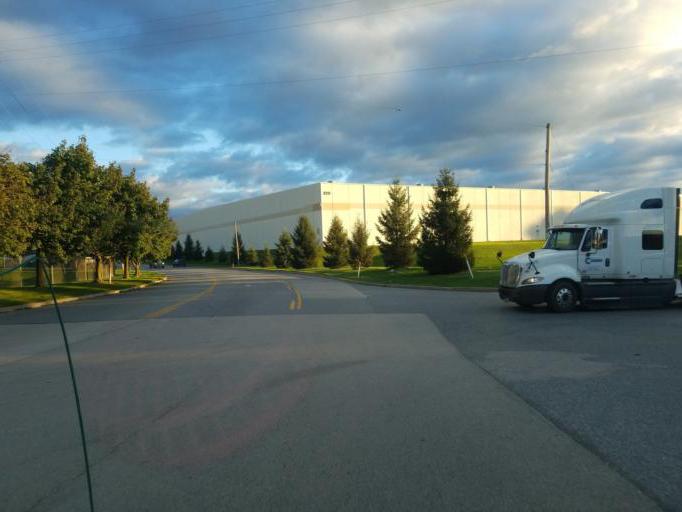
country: US
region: Pennsylvania
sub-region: York County
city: Weigelstown
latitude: 39.9303
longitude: -76.8227
